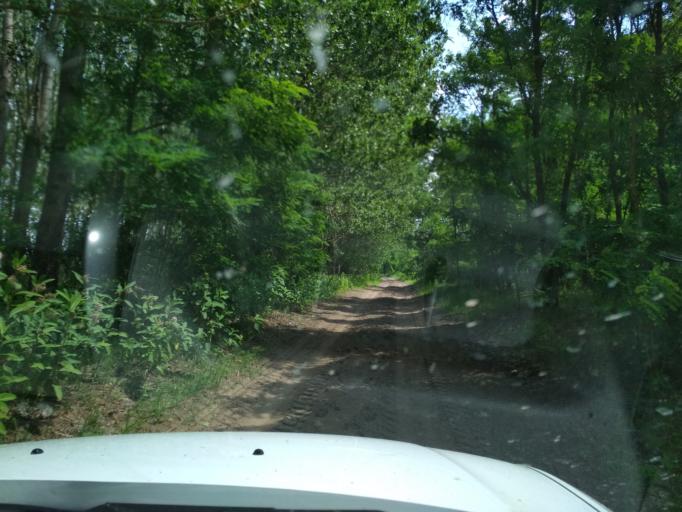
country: HU
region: Pest
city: Tapioszentmarton
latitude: 47.3594
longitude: 19.7448
